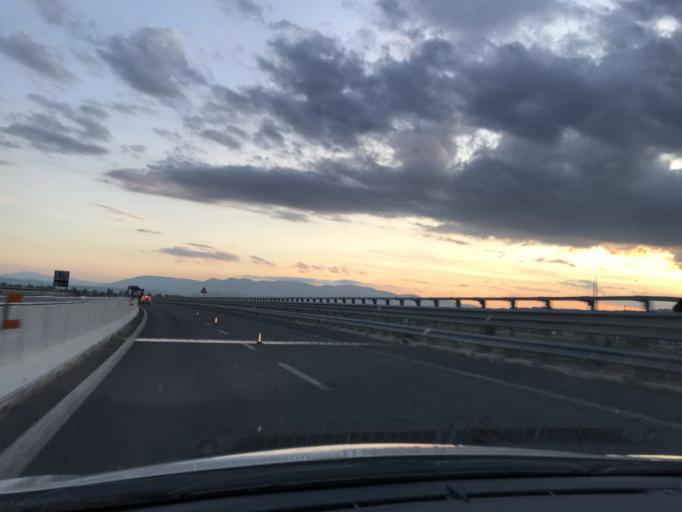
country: IT
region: Umbria
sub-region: Provincia di Perugia
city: Trevi
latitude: 42.9063
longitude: 12.7222
